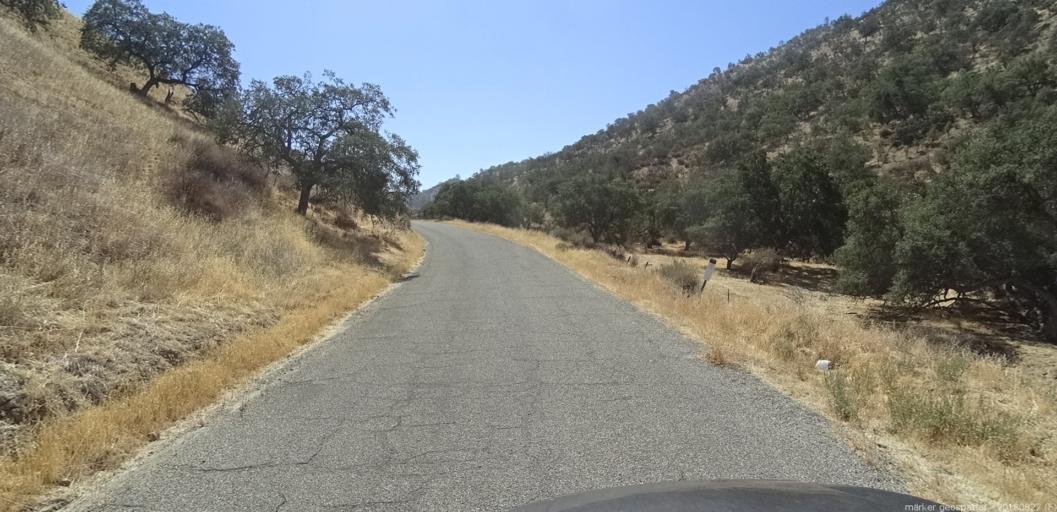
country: US
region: California
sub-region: Monterey County
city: King City
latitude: 36.2990
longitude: -120.9036
